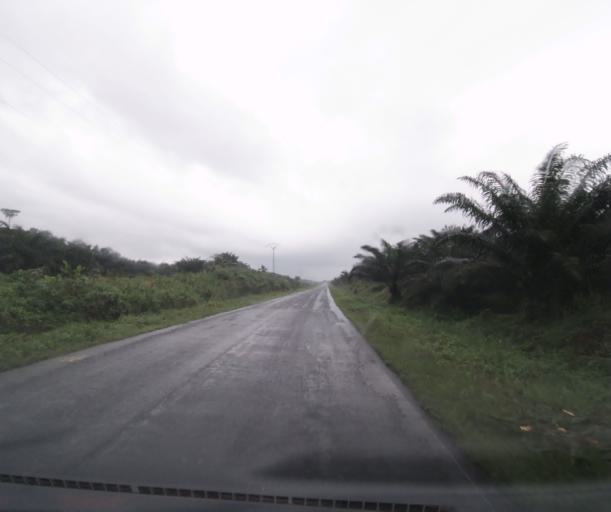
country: CM
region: South-West Province
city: Idenao
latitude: 4.1599
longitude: 8.9936
